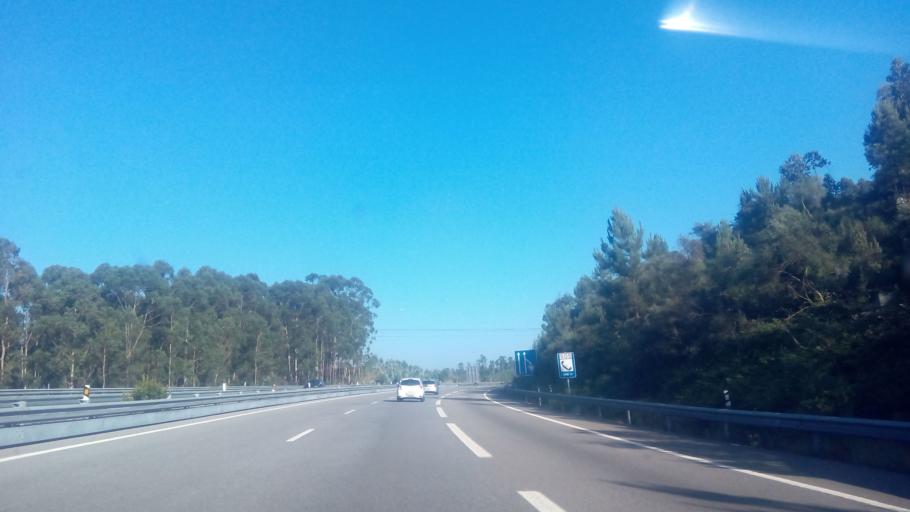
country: PT
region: Porto
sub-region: Pacos de Ferreira
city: Pacos de Ferreira
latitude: 41.2640
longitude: -8.3770
